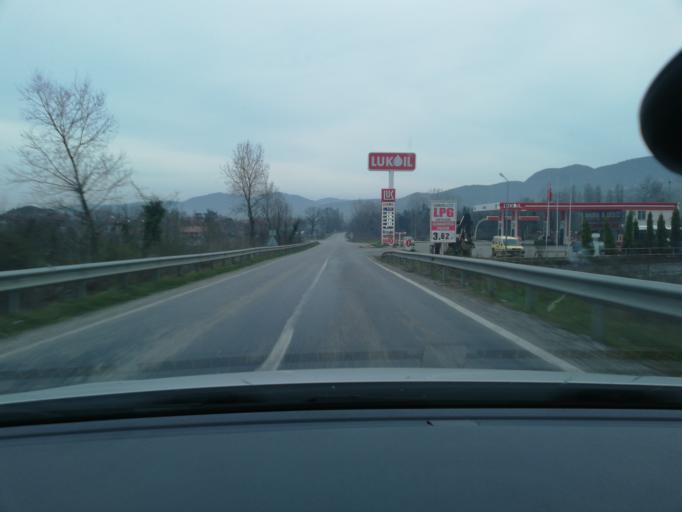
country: TR
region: Zonguldak
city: Saltukova
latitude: 41.5242
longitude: 32.0935
